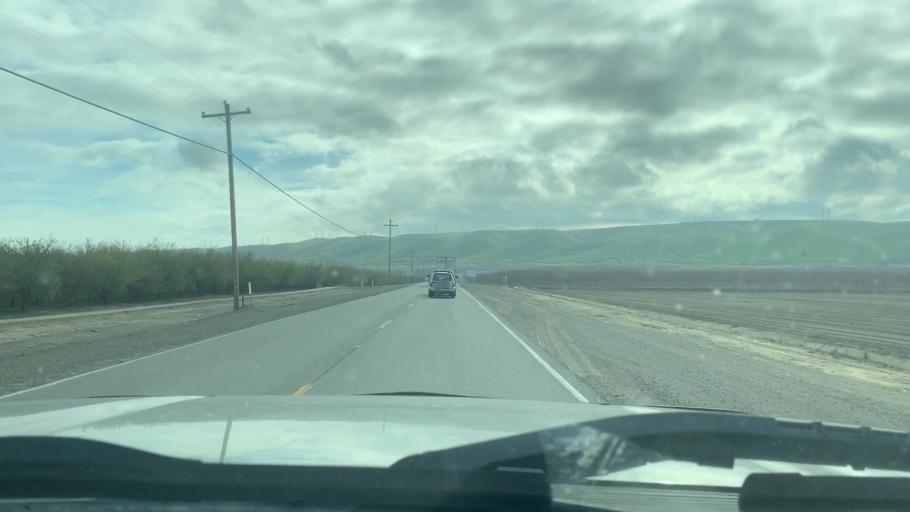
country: US
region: California
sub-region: Merced County
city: Los Banos
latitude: 36.9416
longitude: -120.8379
